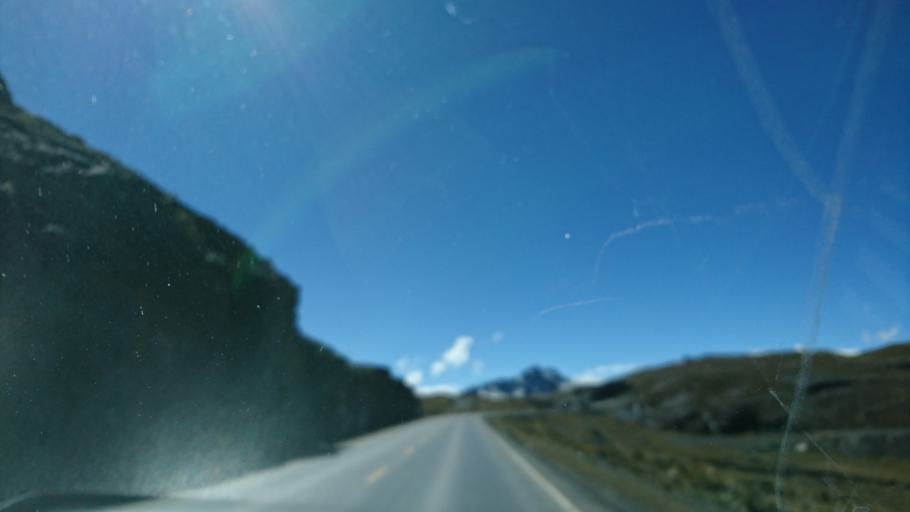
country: BO
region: La Paz
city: La Paz
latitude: -16.3687
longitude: -68.0452
